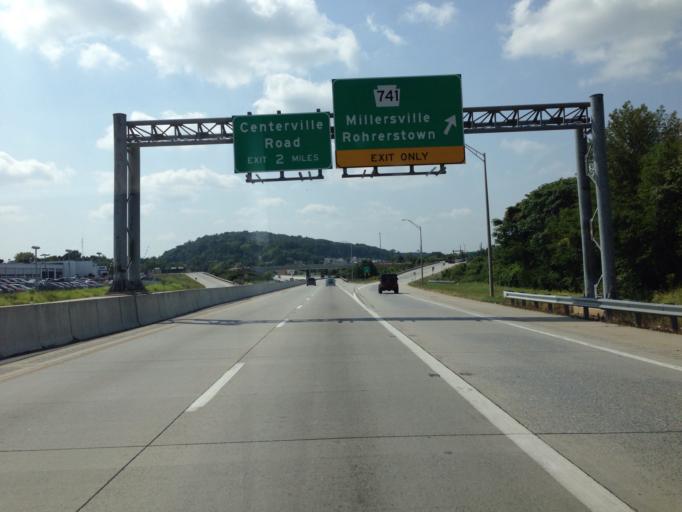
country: US
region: Pennsylvania
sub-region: Lancaster County
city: East Petersburg
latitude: 40.0612
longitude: -76.3557
